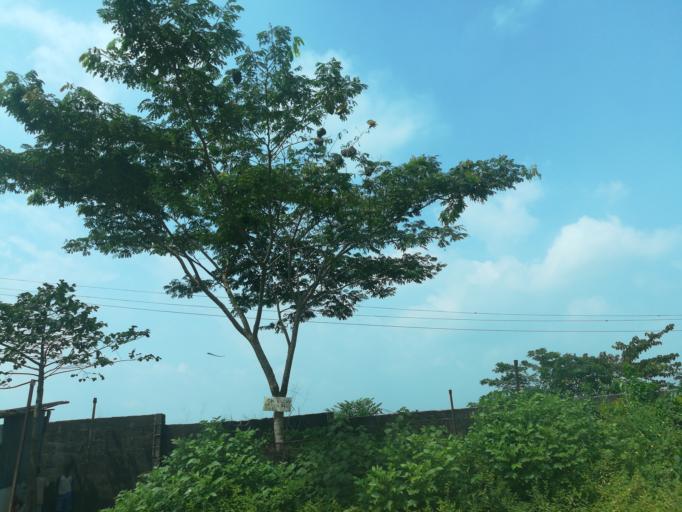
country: NG
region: Lagos
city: Ikorodu
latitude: 6.5939
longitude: 3.6378
